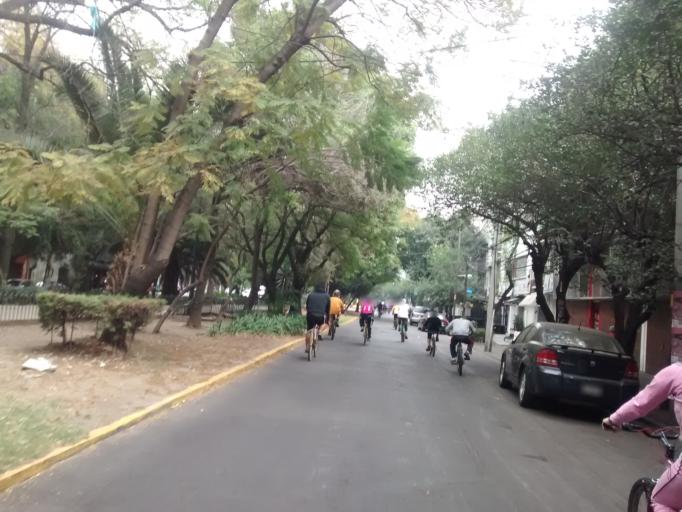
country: MX
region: Mexico City
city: Polanco
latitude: 19.4104
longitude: -99.1791
